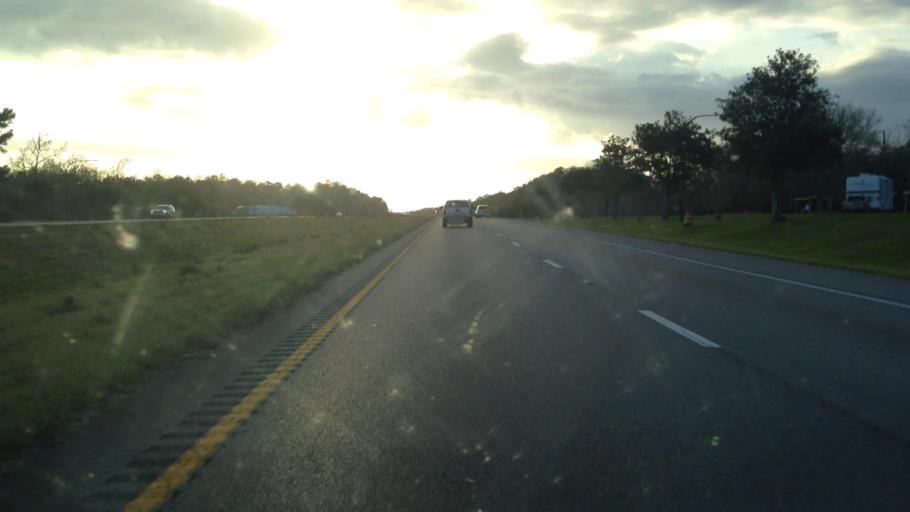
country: US
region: Mississippi
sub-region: Jackson County
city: Hickory Hills
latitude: 30.4380
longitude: -88.6188
